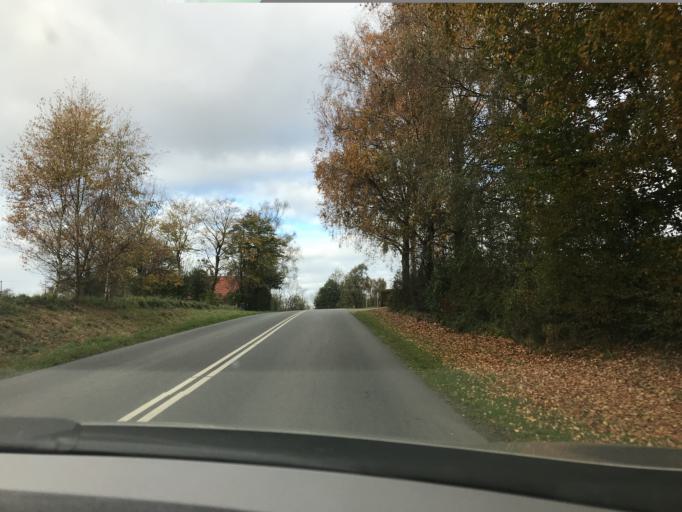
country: DK
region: South Denmark
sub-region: Vejle Kommune
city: Egtved
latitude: 55.5711
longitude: 9.3956
